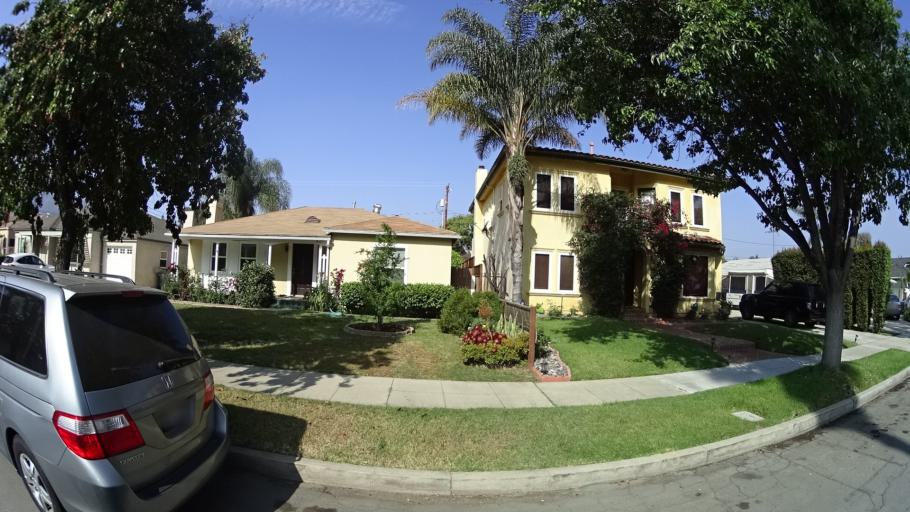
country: US
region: California
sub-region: Los Angeles County
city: Burbank
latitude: 34.1611
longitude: -118.3224
